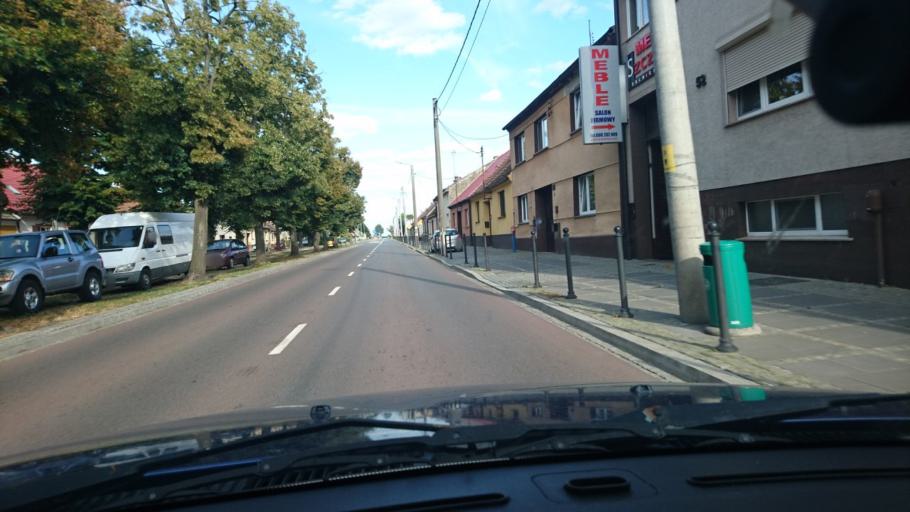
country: PL
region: Greater Poland Voivodeship
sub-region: Powiat krotoszynski
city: Sulmierzyce
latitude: 51.6057
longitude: 17.5357
